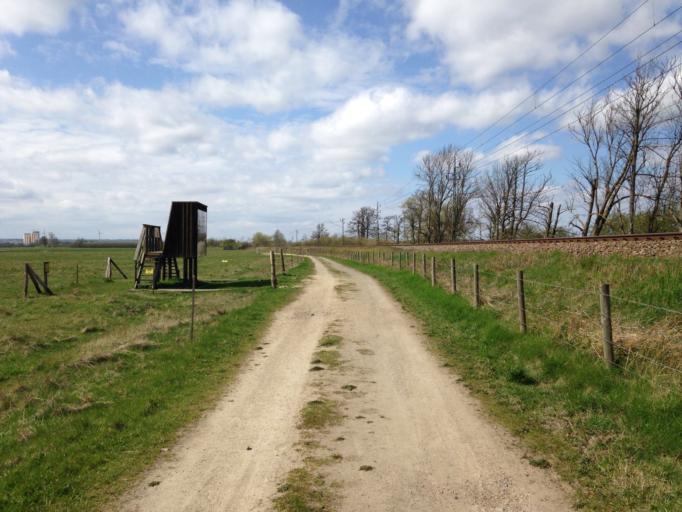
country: SE
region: Skane
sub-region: Kristianstads Kommun
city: Kristianstad
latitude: 56.0415
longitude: 14.1375
